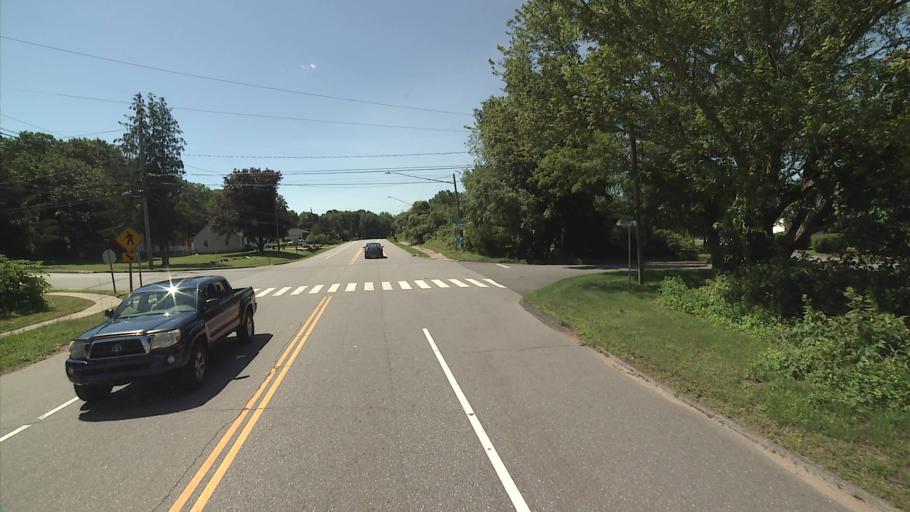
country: US
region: Connecticut
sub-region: New London County
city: Noank
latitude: 41.3312
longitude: -71.9993
